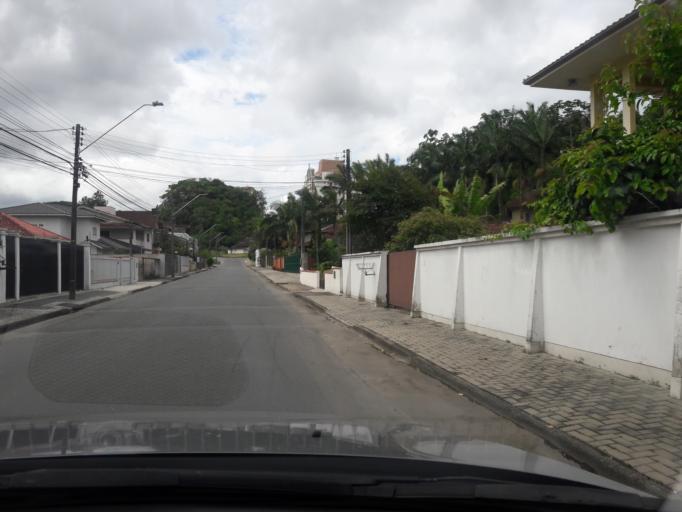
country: BR
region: Santa Catarina
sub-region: Joinville
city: Joinville
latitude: -26.3233
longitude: -48.8652
